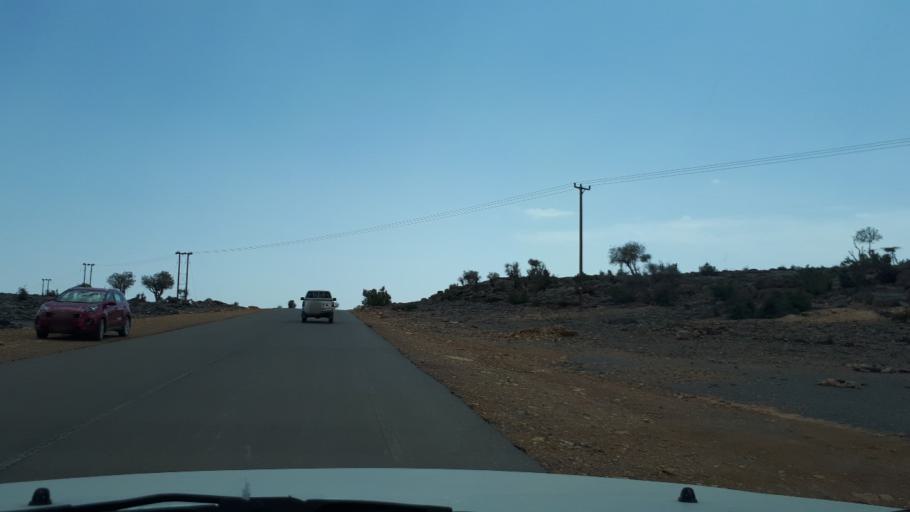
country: OM
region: Muhafazat ad Dakhiliyah
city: Bahla'
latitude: 23.2114
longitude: 57.2035
